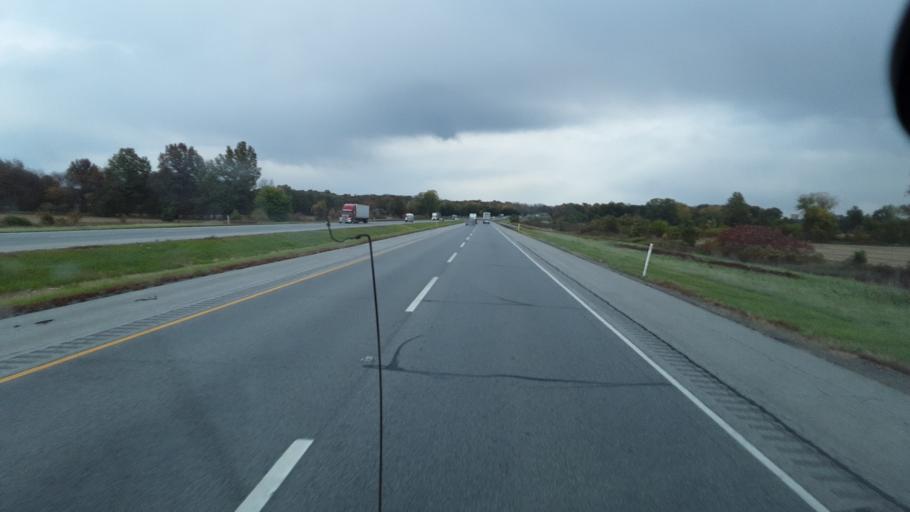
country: US
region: Michigan
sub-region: Berrien County
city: Buchanan
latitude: 41.7498
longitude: -86.4214
